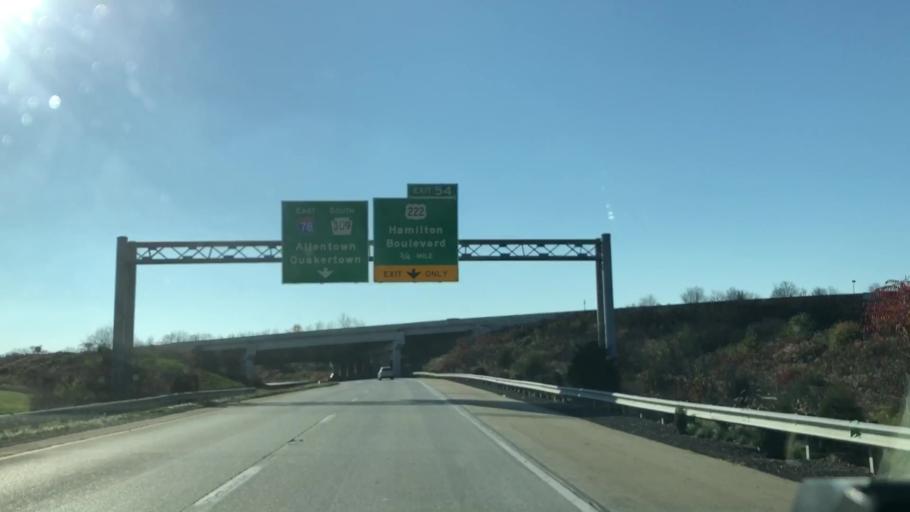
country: US
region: Pennsylvania
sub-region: Lehigh County
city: Wescosville
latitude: 40.5794
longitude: -75.5525
